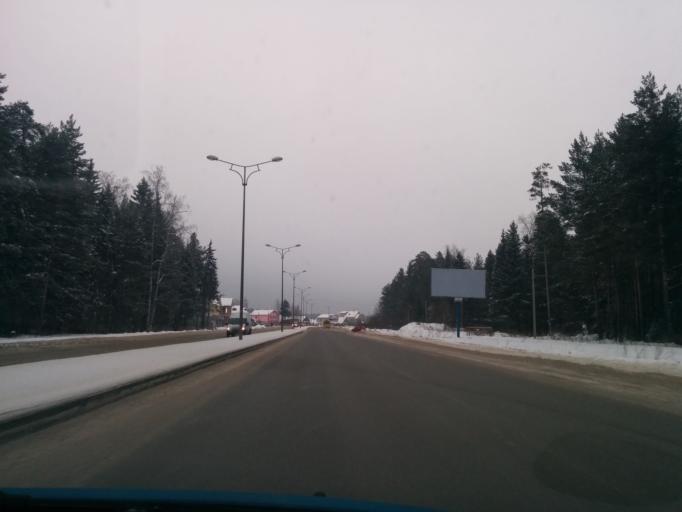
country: RU
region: Perm
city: Kondratovo
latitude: 58.0238
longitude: 55.9960
